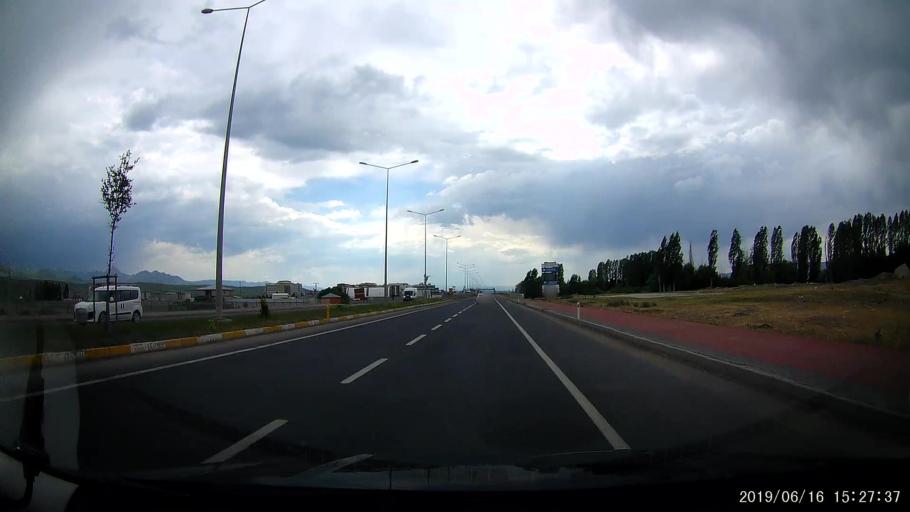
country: TR
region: Erzurum
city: Horasan
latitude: 40.0345
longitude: 42.1556
